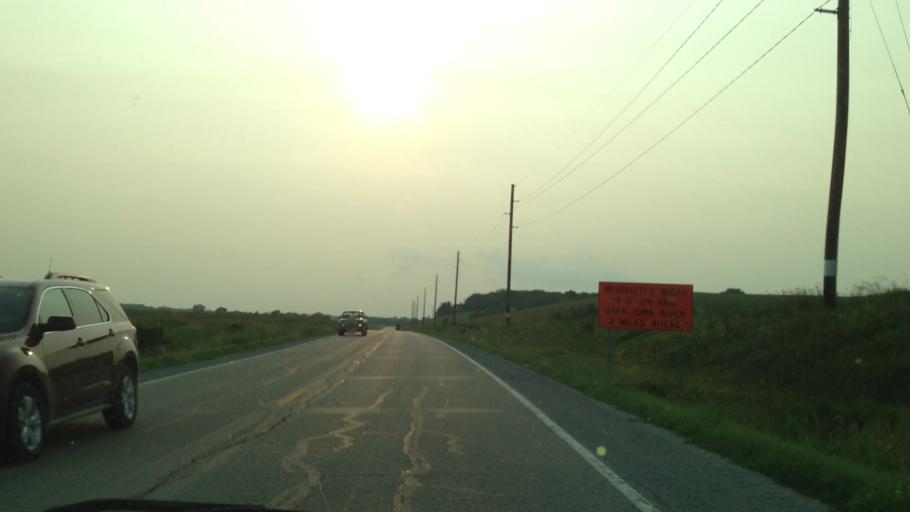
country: US
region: Iowa
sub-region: Benton County
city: Walford
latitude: 41.7976
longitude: -91.9182
